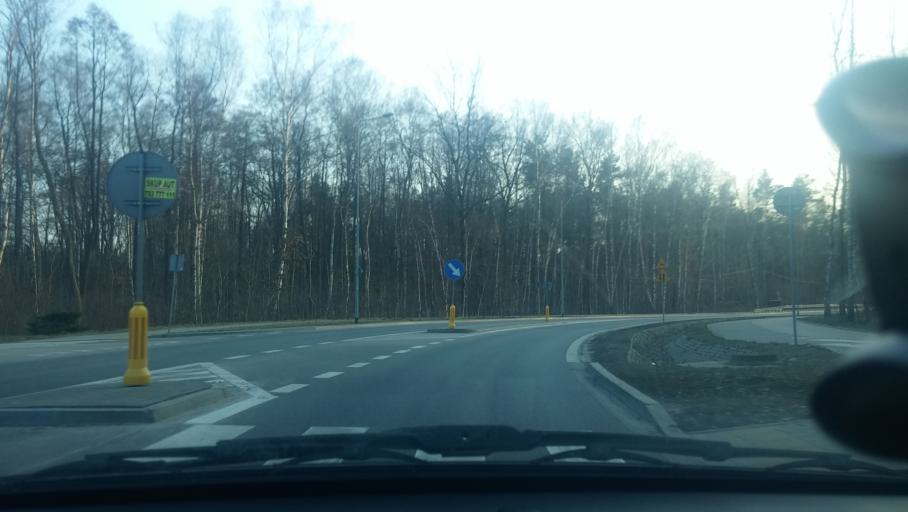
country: PL
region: Masovian Voivodeship
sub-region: Warszawa
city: Wesola
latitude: 52.2143
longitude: 21.2178
